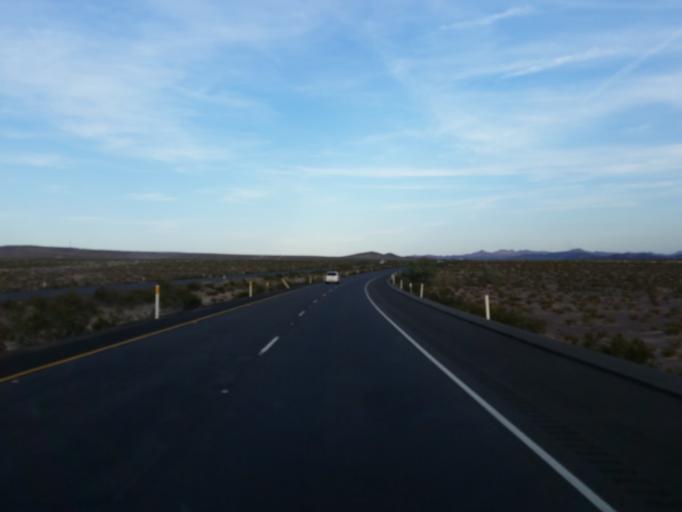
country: US
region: California
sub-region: San Bernardino County
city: Fort Irwin
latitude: 34.7710
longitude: -116.3644
